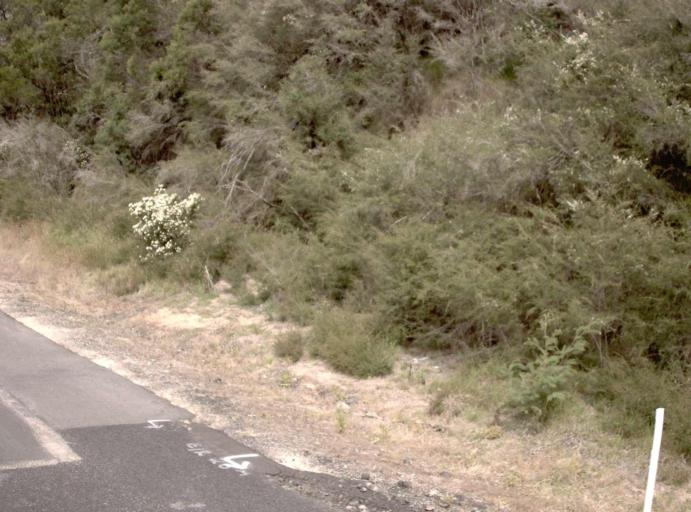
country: AU
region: New South Wales
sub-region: Bega Valley
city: Eden
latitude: -37.4778
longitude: 149.6121
